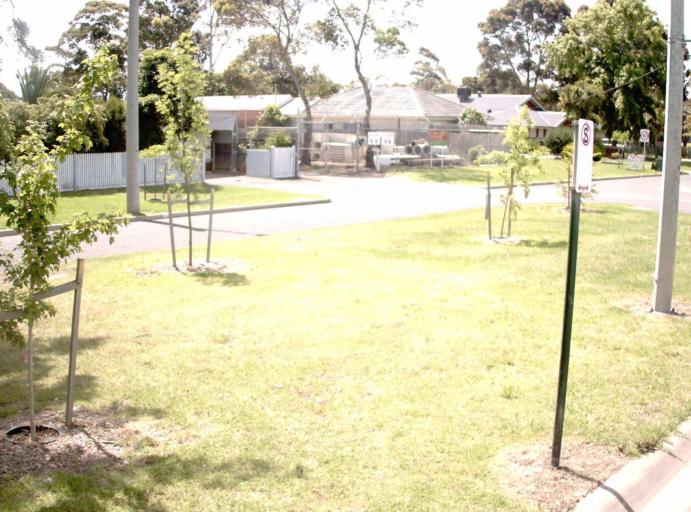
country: AU
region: Victoria
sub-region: Wellington
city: Sale
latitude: -38.0962
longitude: 147.0683
